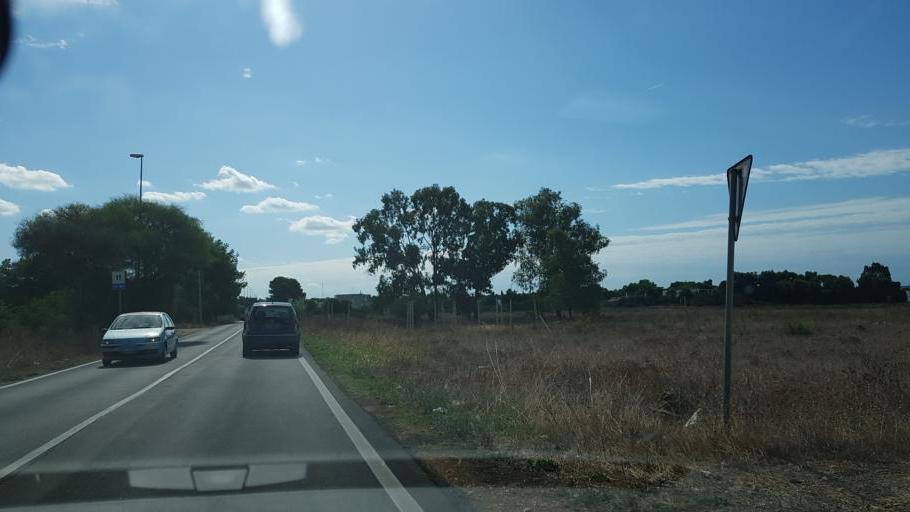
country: IT
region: Apulia
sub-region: Provincia di Lecce
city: Porto Cesareo
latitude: 40.2499
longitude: 17.9112
